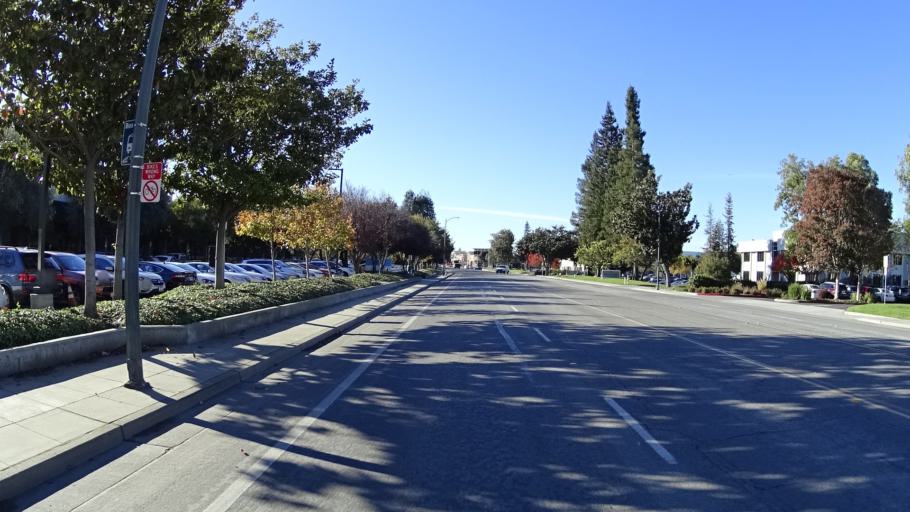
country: US
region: California
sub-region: Santa Clara County
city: Sunnyvale
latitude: 37.3806
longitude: -122.0043
